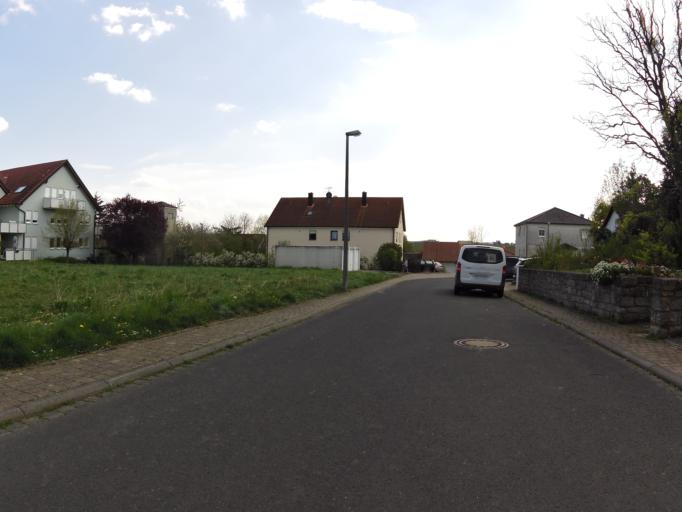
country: DE
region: Bavaria
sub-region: Regierungsbezirk Unterfranken
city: Giebelstadt
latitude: 49.6702
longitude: 9.9551
